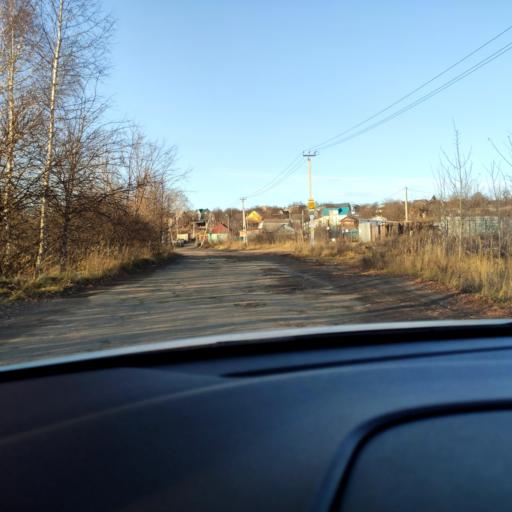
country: RU
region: Tatarstan
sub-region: Gorod Kazan'
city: Kazan
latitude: 55.8839
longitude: 49.0693
